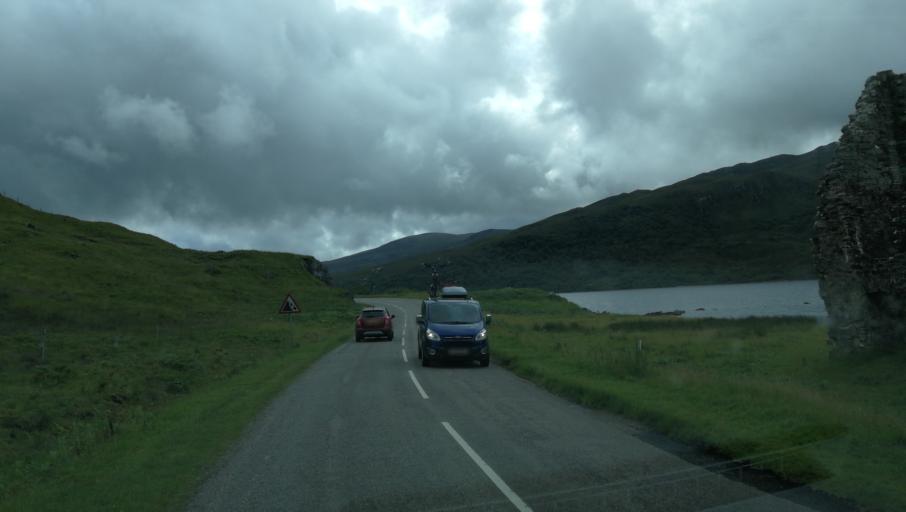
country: GB
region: Scotland
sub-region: Highland
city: Ullapool
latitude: 58.1641
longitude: -4.9864
